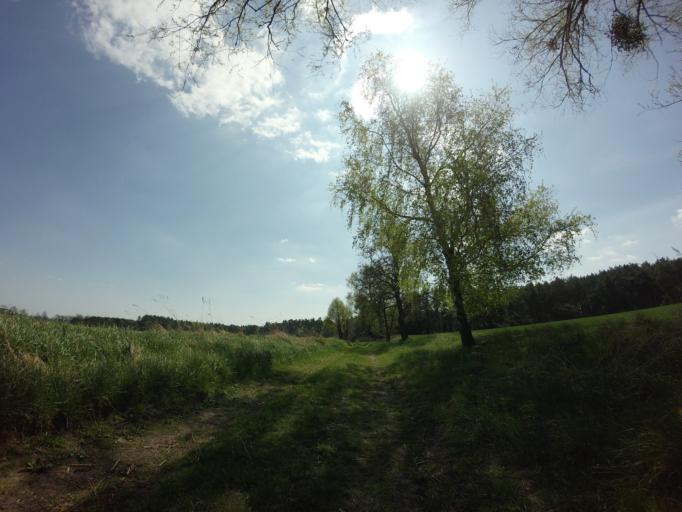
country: PL
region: West Pomeranian Voivodeship
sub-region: Powiat stargardzki
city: Suchan
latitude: 53.2201
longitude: 15.3007
